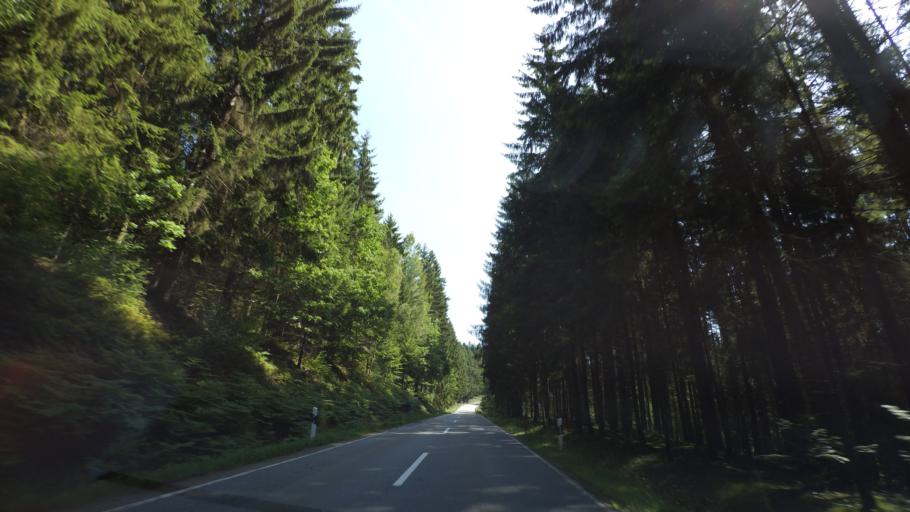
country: DE
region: Bavaria
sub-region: Lower Bavaria
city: Geiersthal
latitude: 49.0533
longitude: 12.9963
